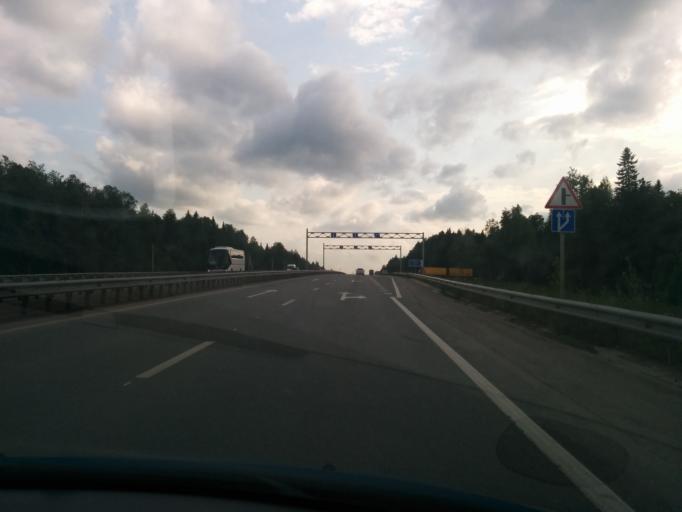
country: RU
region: Perm
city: Ferma
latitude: 58.0277
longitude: 56.4290
